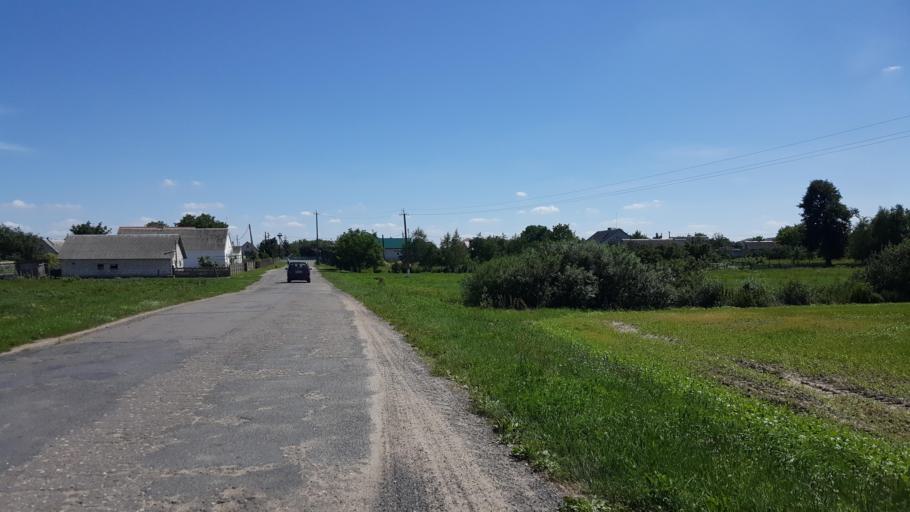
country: BY
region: Brest
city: Charnawchytsy
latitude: 52.2676
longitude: 23.5805
